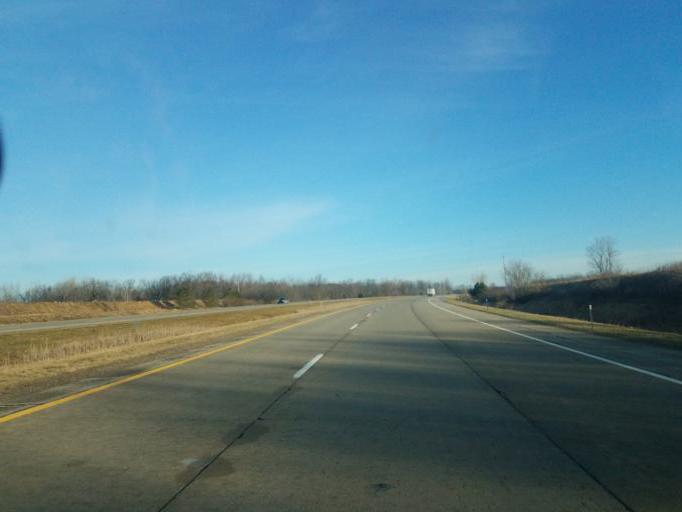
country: US
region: Michigan
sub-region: Clinton County
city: DeWitt
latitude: 42.8254
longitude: -84.5175
